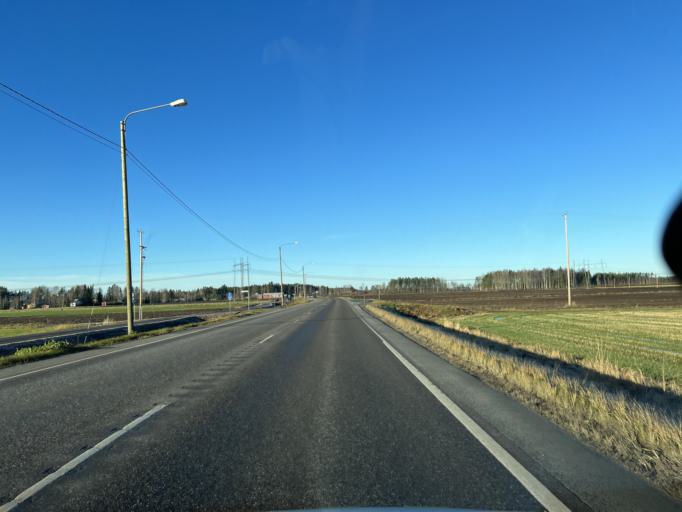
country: FI
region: Northern Ostrobothnia
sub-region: Nivala-Haapajaervi
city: Nivala
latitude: 63.9523
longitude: 24.8755
